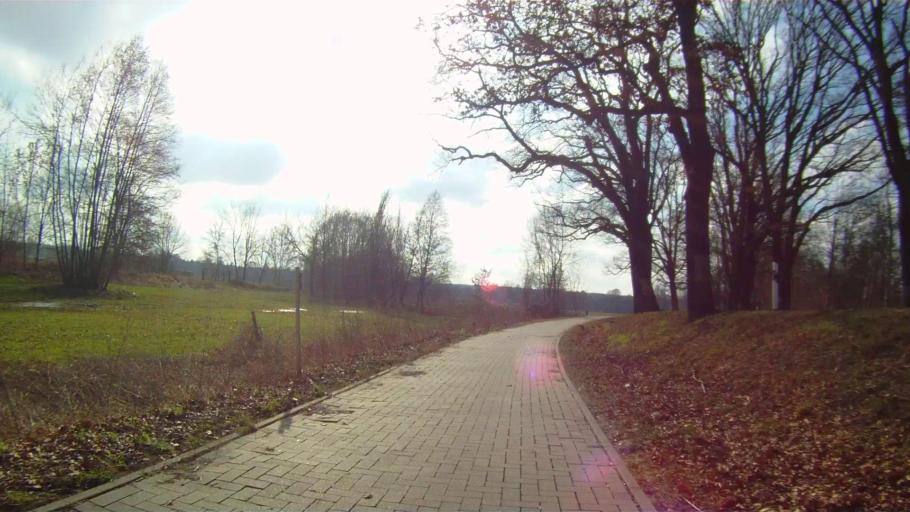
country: DE
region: Brandenburg
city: Erkner
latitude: 52.3958
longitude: 13.7478
